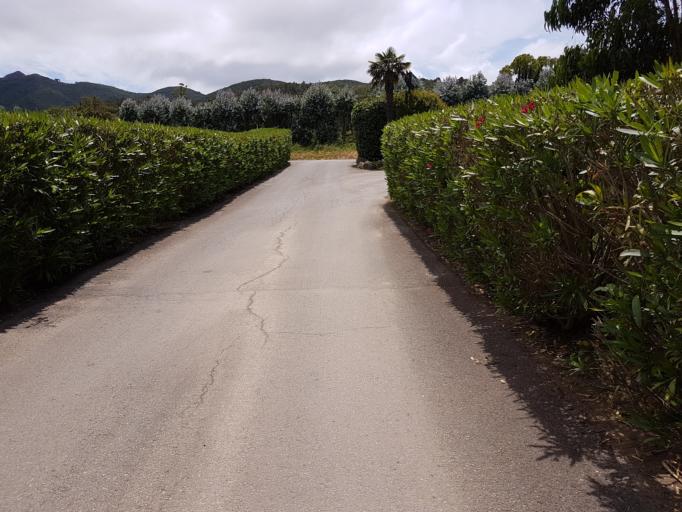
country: IT
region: Tuscany
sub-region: Provincia di Livorno
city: Portoferraio
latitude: 42.7950
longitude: 10.3553
